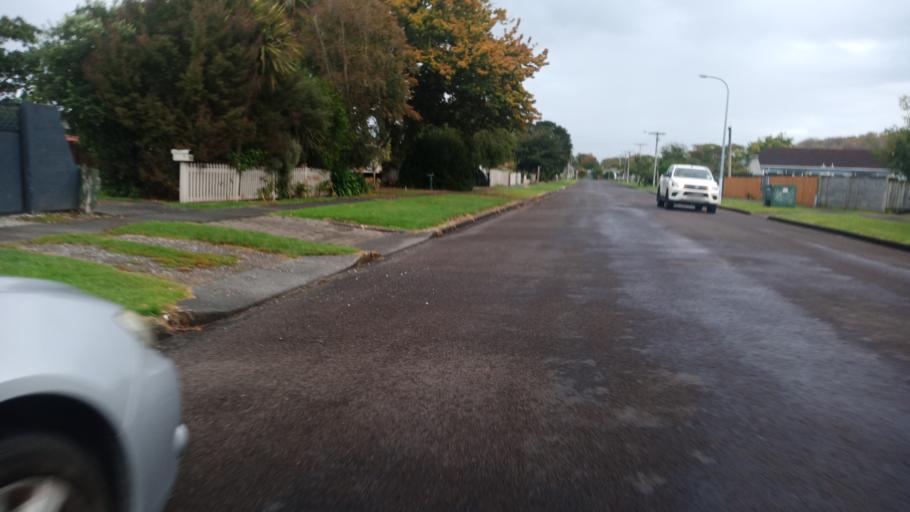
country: NZ
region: Gisborne
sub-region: Gisborne District
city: Gisborne
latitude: -38.6425
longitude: 178.0114
